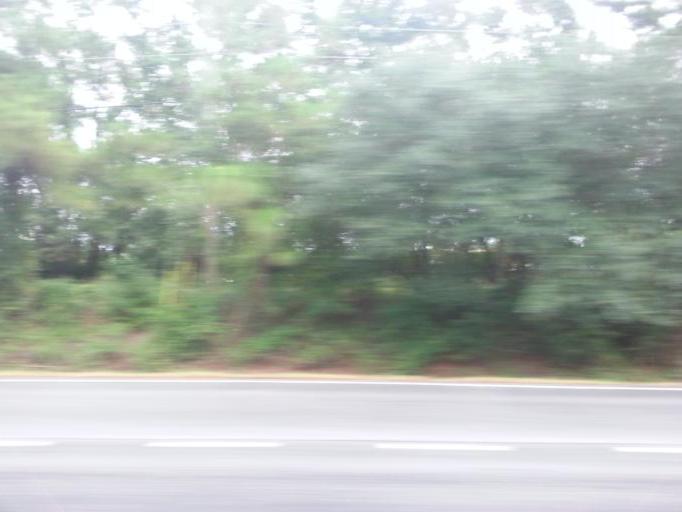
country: US
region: Alabama
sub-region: Baldwin County
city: Fairhope
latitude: 30.5551
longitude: -87.8928
